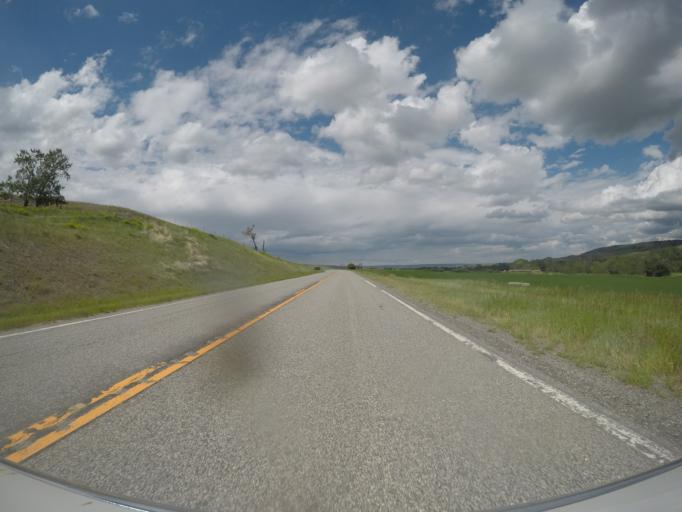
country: US
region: Montana
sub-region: Sweet Grass County
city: Big Timber
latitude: 45.7572
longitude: -109.9913
